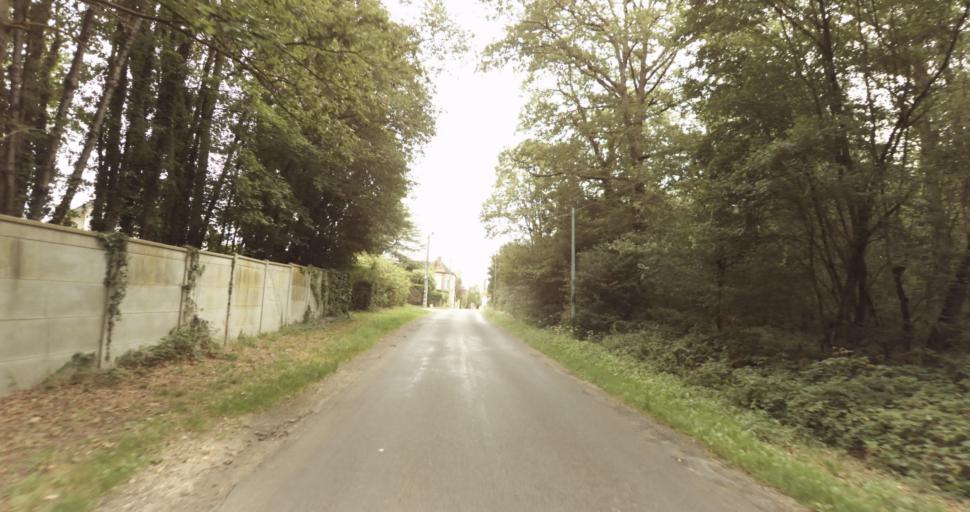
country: FR
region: Haute-Normandie
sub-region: Departement de l'Eure
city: La Couture-Boussey
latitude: 48.8871
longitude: 1.3812
